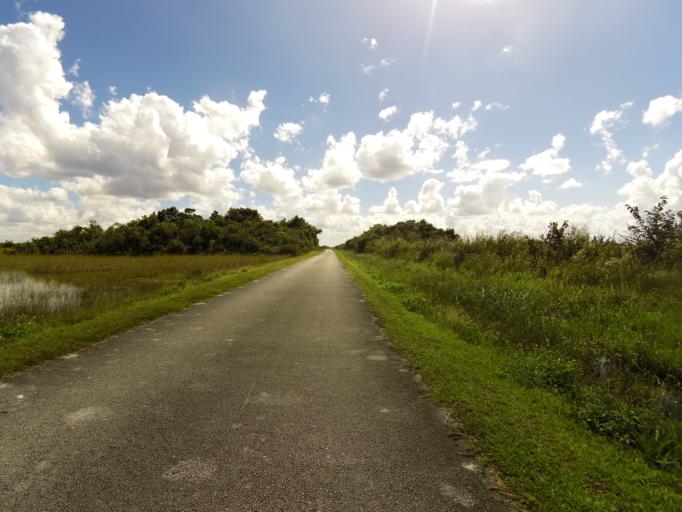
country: US
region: Florida
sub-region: Miami-Dade County
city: The Hammocks
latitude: 25.7100
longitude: -80.7668
